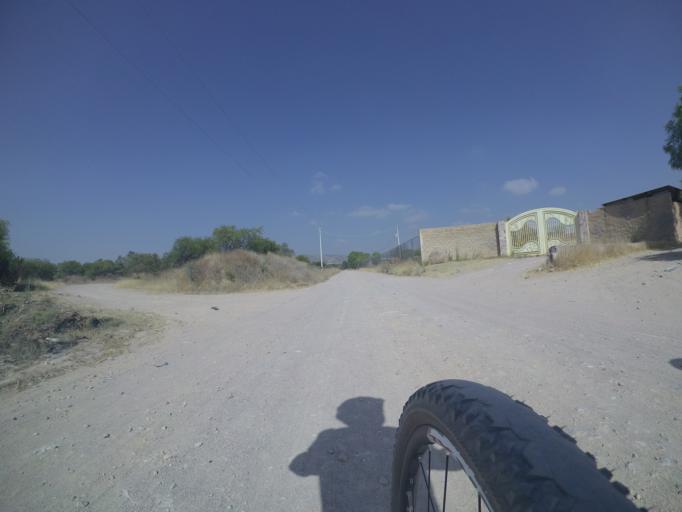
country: MX
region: Aguascalientes
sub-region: Jesus Maria
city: Paseos de las Haciendas [Fraccionamiento]
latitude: 21.9991
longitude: -102.3426
